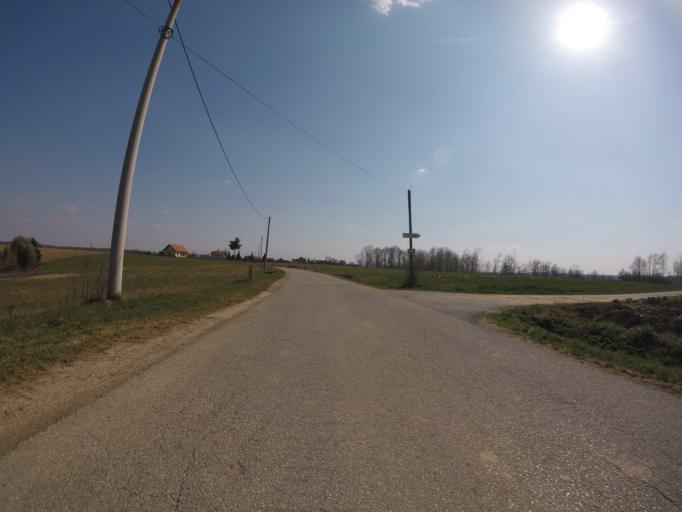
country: HR
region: Grad Zagreb
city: Strmec
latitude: 45.5237
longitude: 15.9234
